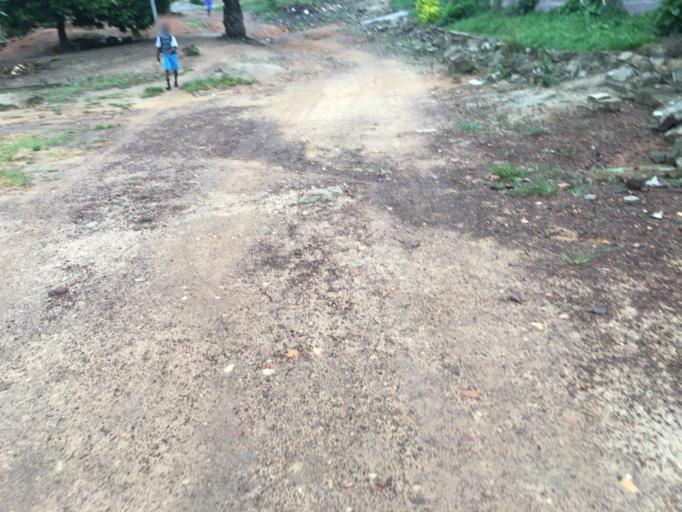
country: GH
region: Ashanti
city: Tafo
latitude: 6.7498
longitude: -1.5982
